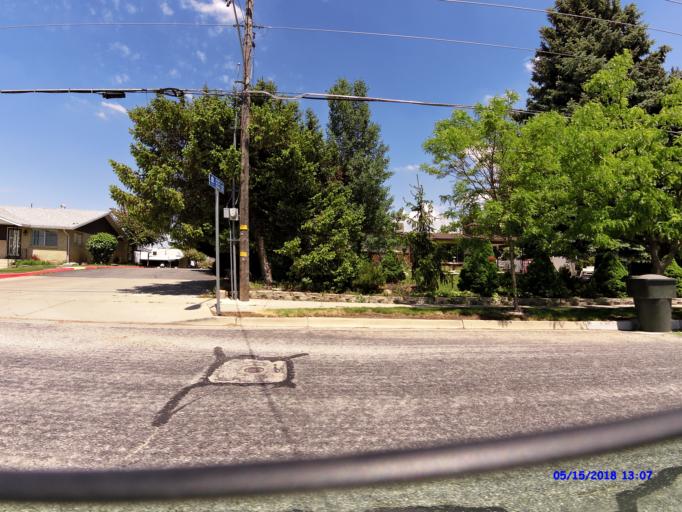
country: US
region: Utah
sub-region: Weber County
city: South Ogden
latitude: 41.1886
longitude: -111.9557
